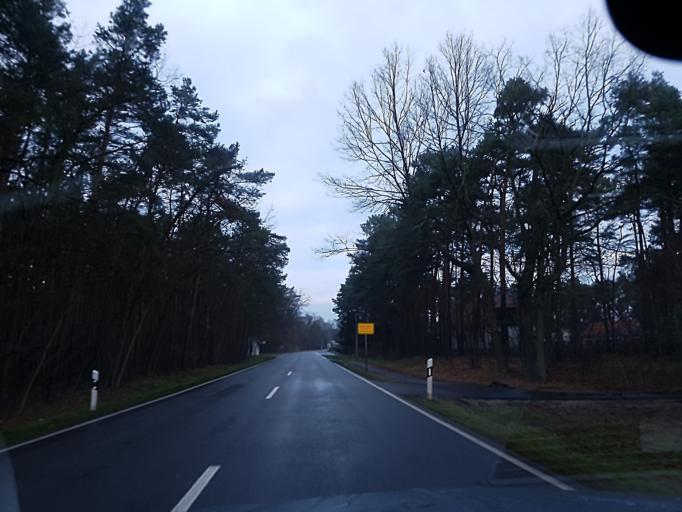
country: DE
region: Brandenburg
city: Schilda
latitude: 51.5861
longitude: 13.3575
